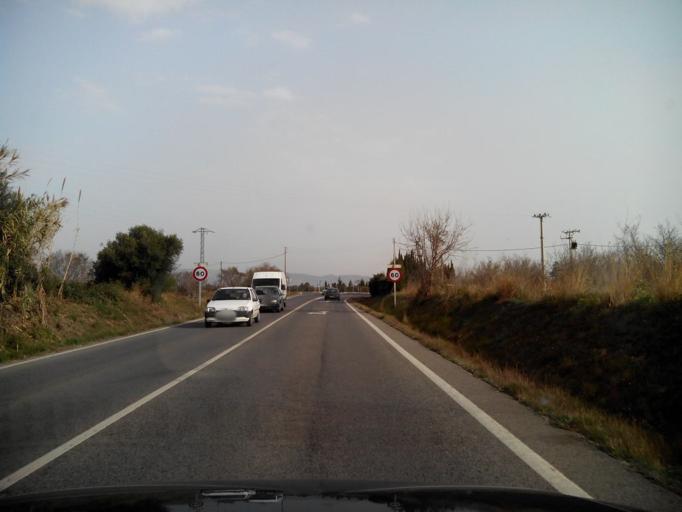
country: ES
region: Catalonia
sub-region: Provincia de Tarragona
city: Cambrils
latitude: 41.1037
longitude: 1.0837
